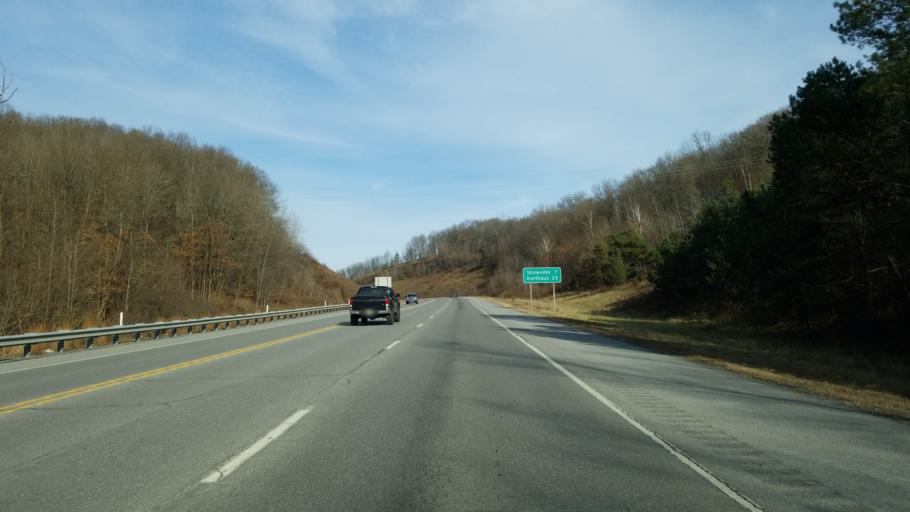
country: US
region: Pennsylvania
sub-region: Clearfield County
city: Clearfield
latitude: 41.0113
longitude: -78.4310
